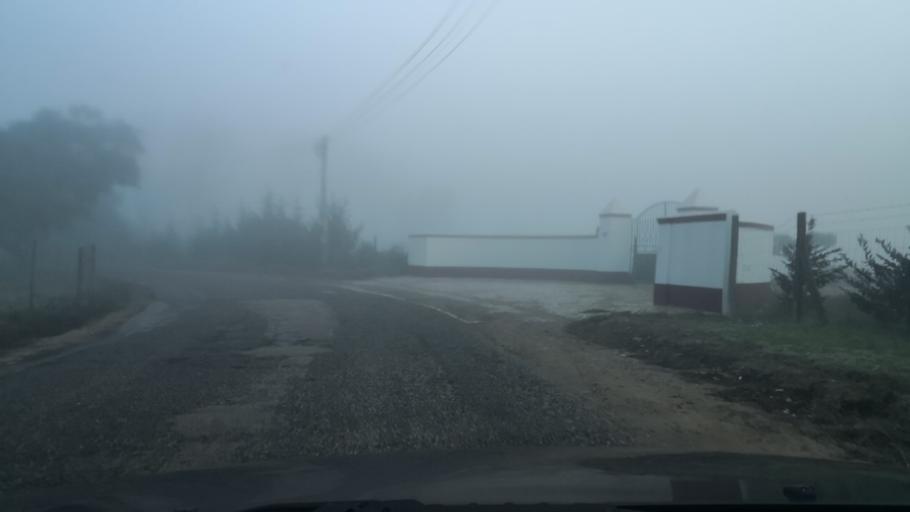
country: PT
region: Setubal
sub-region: Palmela
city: Palmela
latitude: 38.5641
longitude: -8.8358
